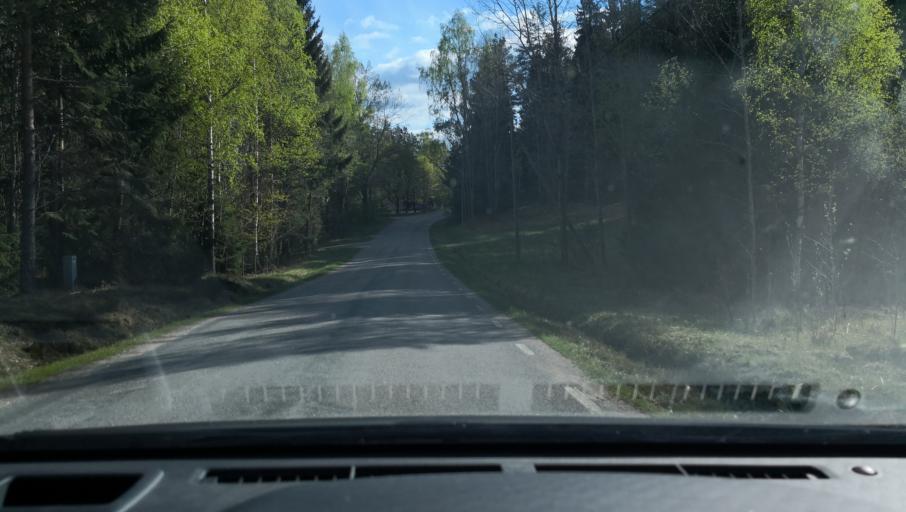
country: SE
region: OErebro
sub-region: Askersunds Kommun
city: Asbro
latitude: 58.9605
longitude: 15.0651
